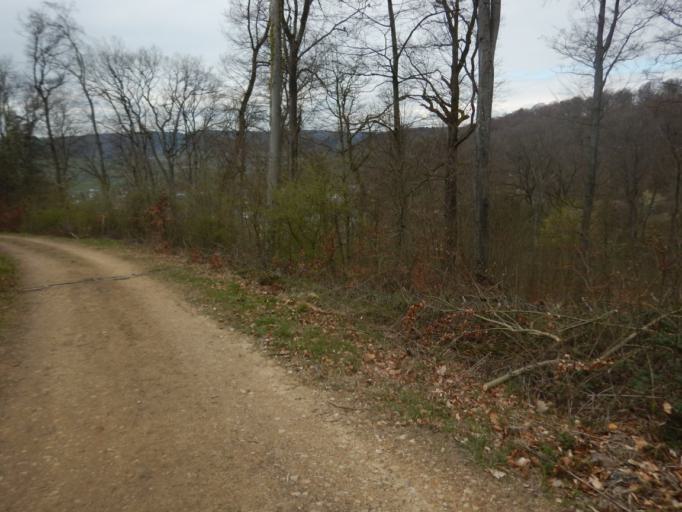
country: LU
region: Luxembourg
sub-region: Canton de Mersch
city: Lorentzweiler
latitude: 49.7007
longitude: 6.1565
